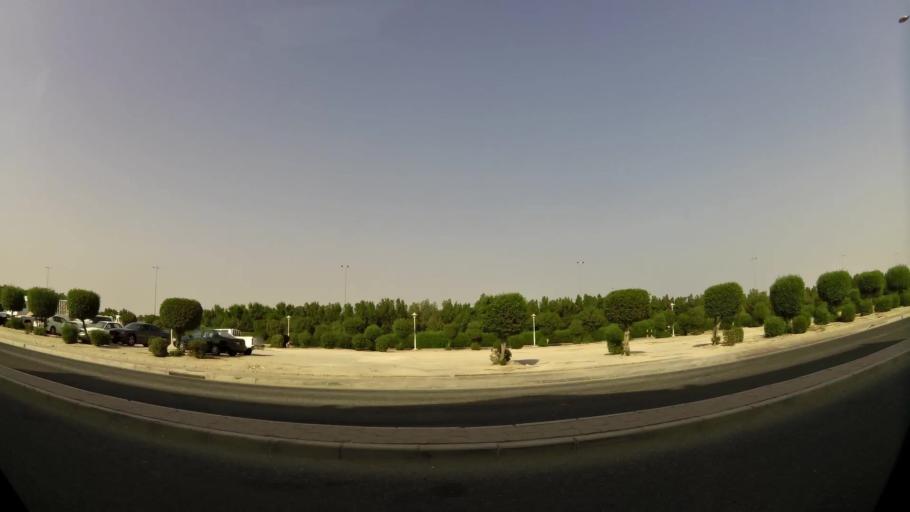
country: KW
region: Muhafazat al Jahra'
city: Al Jahra'
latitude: 29.3481
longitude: 47.6947
